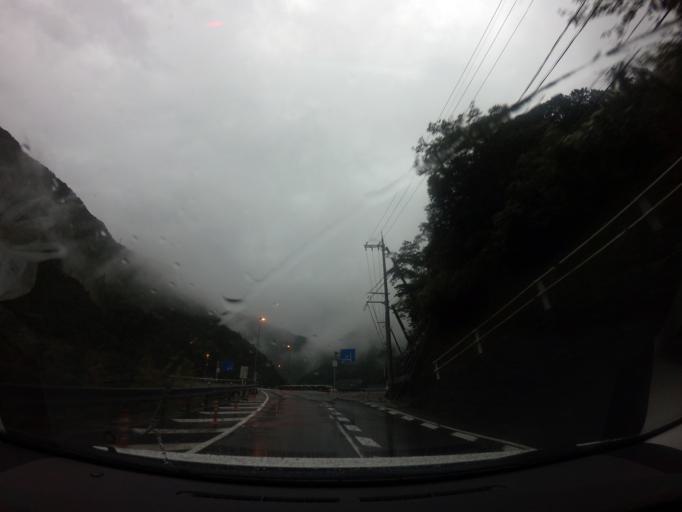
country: JP
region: Wakayama
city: Shingu
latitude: 33.9505
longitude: 135.8006
